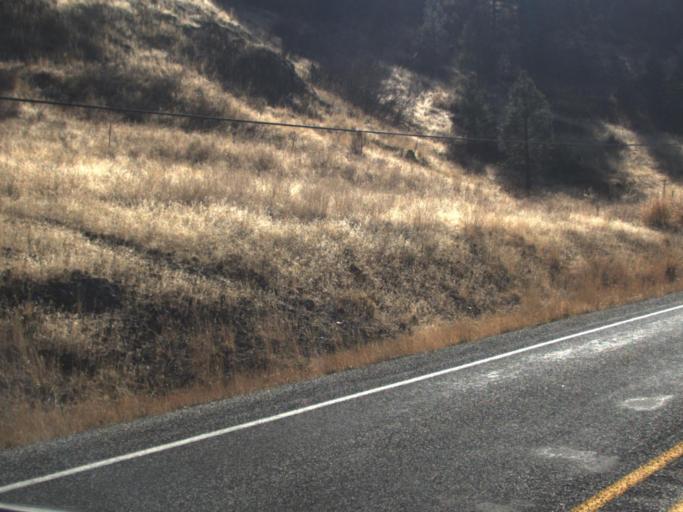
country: US
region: Washington
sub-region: Ferry County
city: Republic
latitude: 48.6715
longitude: -118.6671
